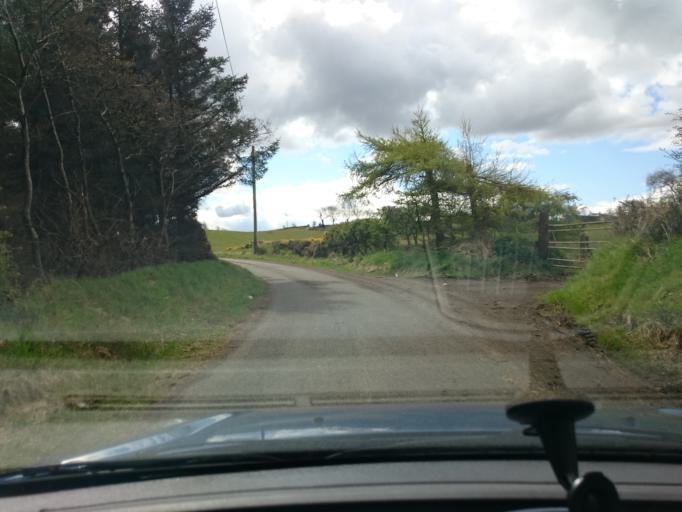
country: GB
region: Scotland
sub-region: Falkirk
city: Bonnybridge
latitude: 55.9818
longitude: -3.8947
